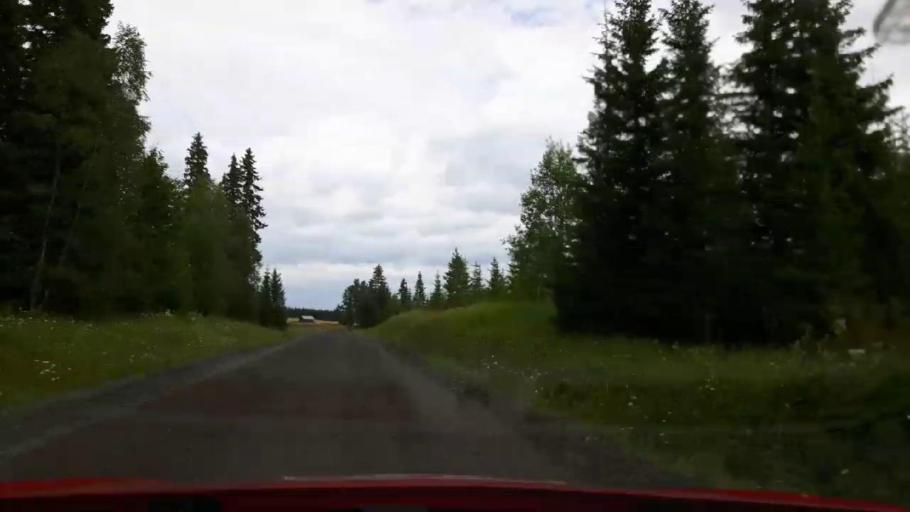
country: SE
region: Jaemtland
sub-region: OEstersunds Kommun
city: Lit
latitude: 63.4374
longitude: 15.2670
